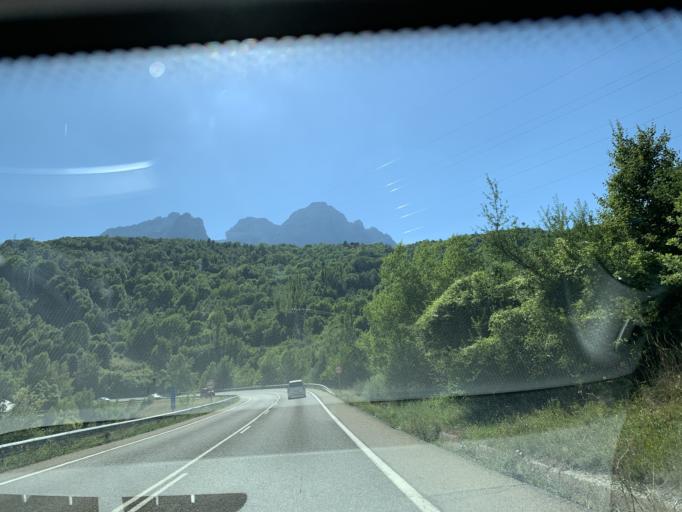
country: ES
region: Aragon
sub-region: Provincia de Huesca
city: Hoz de Jaca
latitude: 42.7040
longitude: -0.3184
